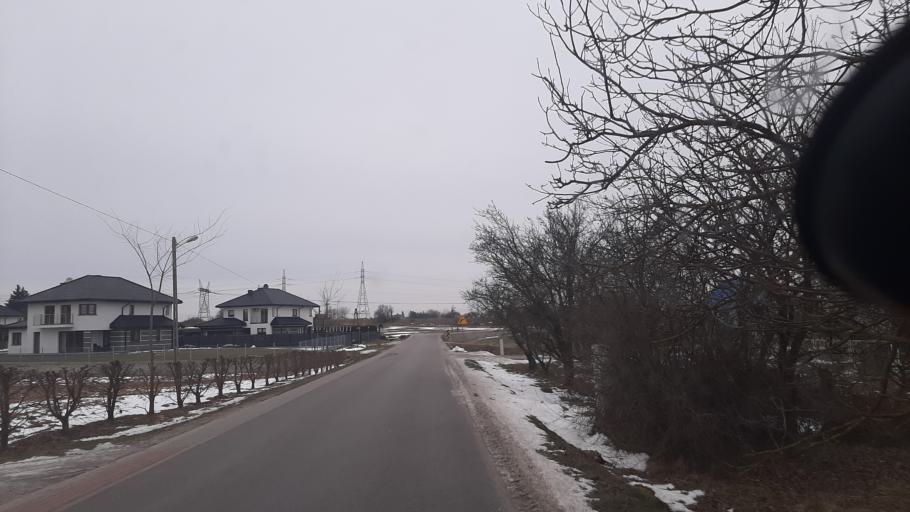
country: PL
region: Lublin Voivodeship
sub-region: Powiat lubelski
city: Jakubowice Murowane
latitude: 51.2922
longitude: 22.6244
